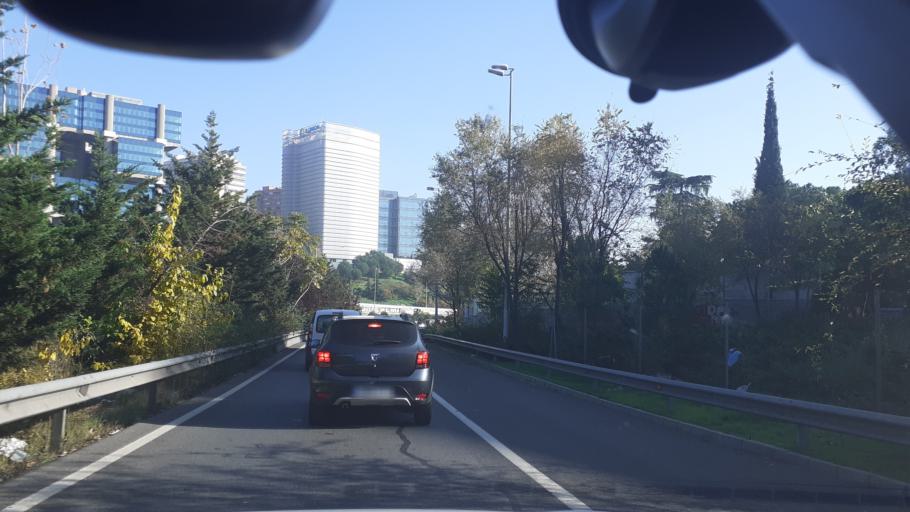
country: ES
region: Madrid
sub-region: Provincia de Madrid
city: Ciudad Lineal
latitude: 40.4433
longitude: -3.6612
